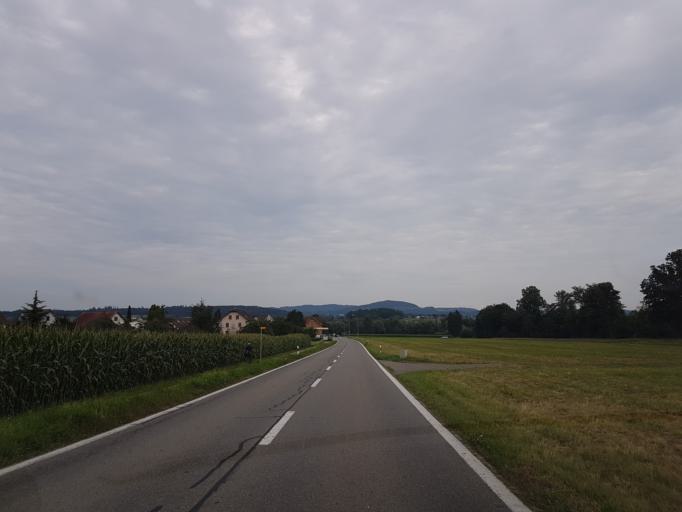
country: CH
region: Aargau
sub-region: Bezirk Muri
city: Merenschwand
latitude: 47.2625
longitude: 8.3908
